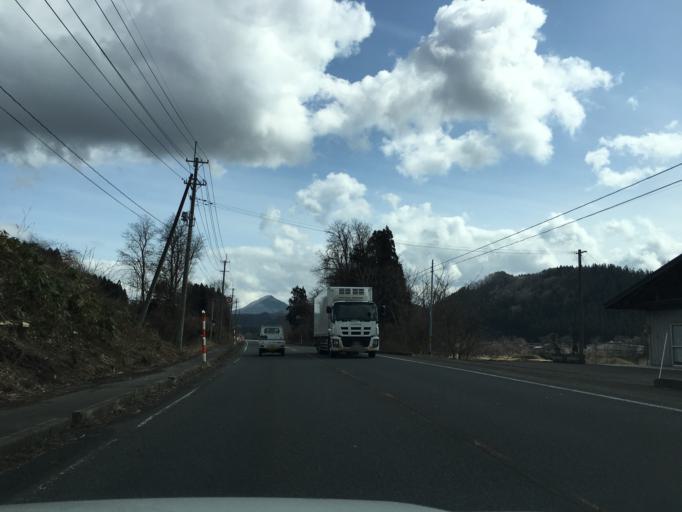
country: JP
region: Akita
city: Odate
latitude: 40.2212
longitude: 140.6076
